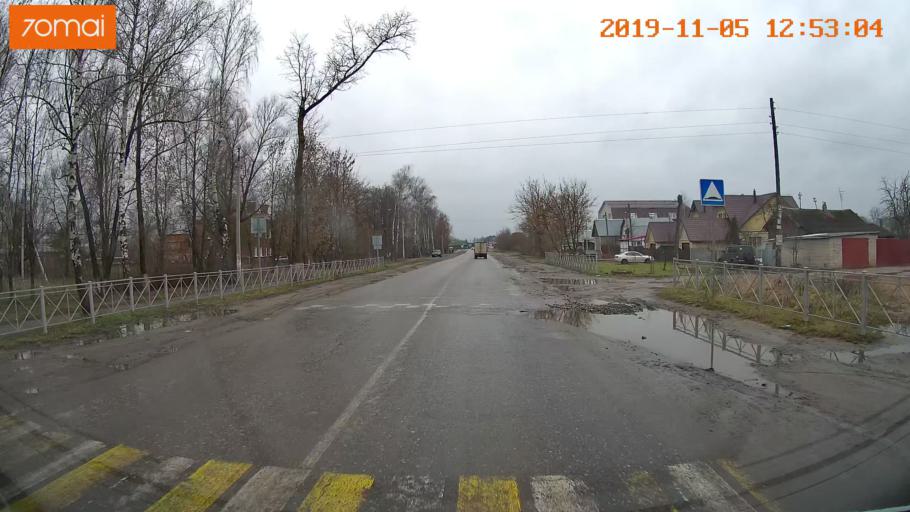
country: RU
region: Ivanovo
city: Kokhma
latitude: 56.9375
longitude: 41.1012
